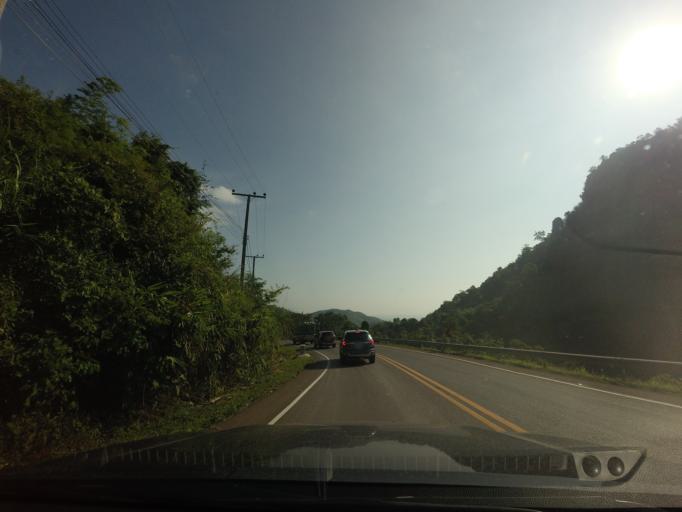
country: TH
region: Phetchabun
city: Lom Kao
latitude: 16.8675
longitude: 101.1422
